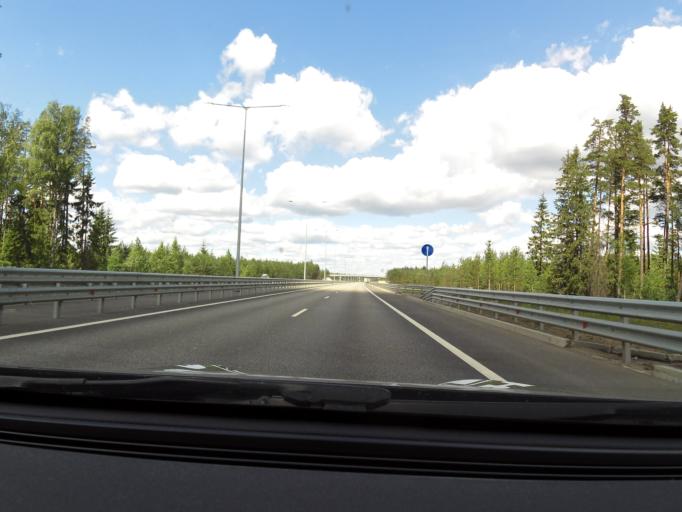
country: RU
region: Tverskaya
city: Krasnomayskiy
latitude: 57.4864
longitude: 34.3174
